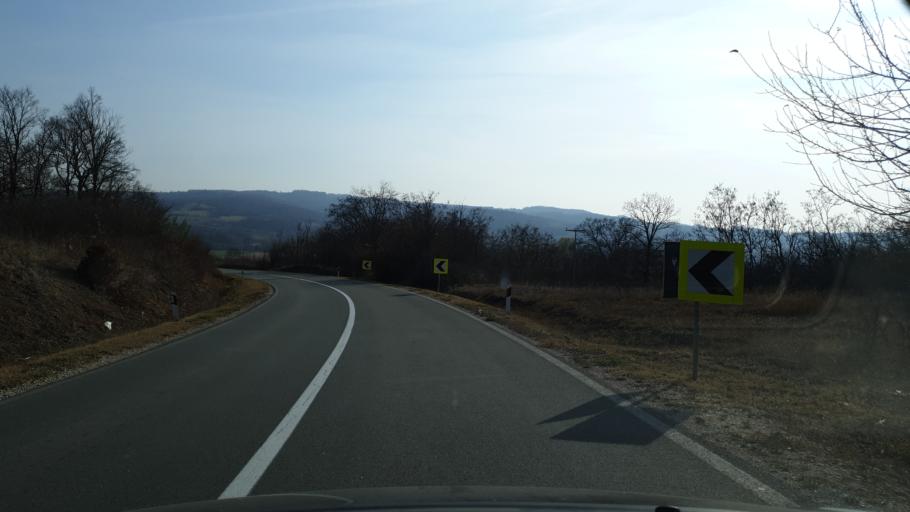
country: RS
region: Central Serbia
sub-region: Borski Okrug
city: Bor
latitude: 43.9335
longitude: 22.0911
